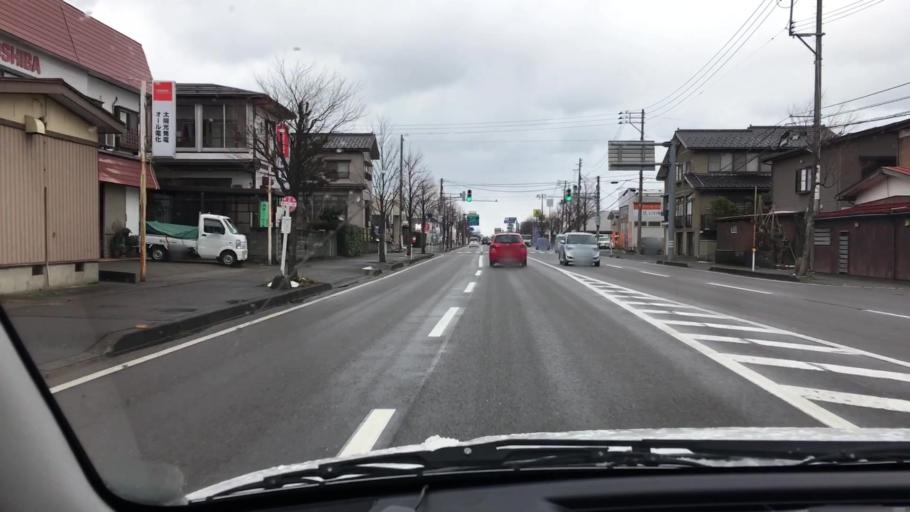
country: JP
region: Niigata
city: Joetsu
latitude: 37.1448
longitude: 138.2284
